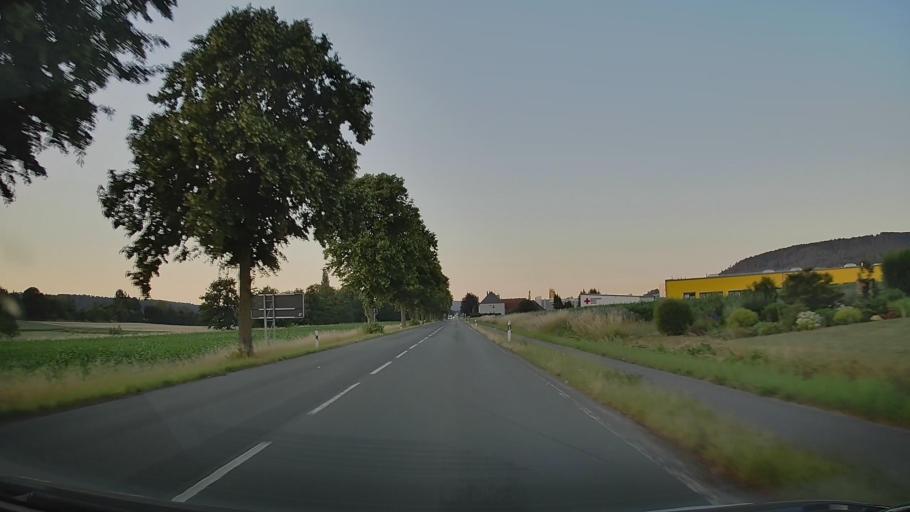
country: DE
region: Lower Saxony
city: Aerzen
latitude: 52.0365
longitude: 9.2481
